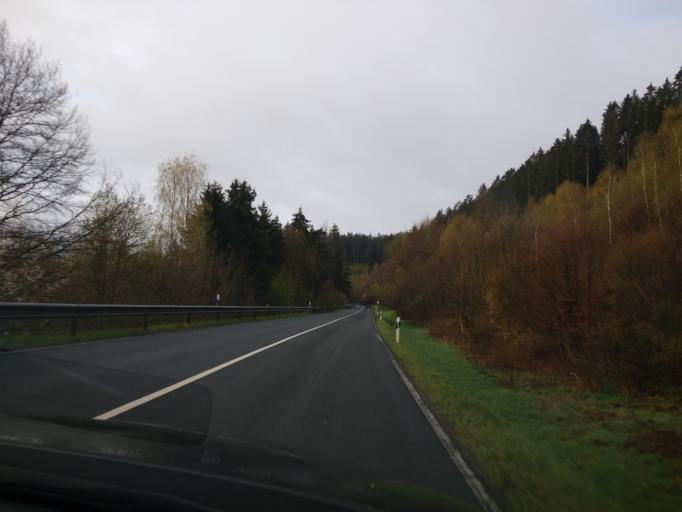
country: DE
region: Rheinland-Pfalz
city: Dohm-Lammersdorf
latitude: 50.2515
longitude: 6.6602
